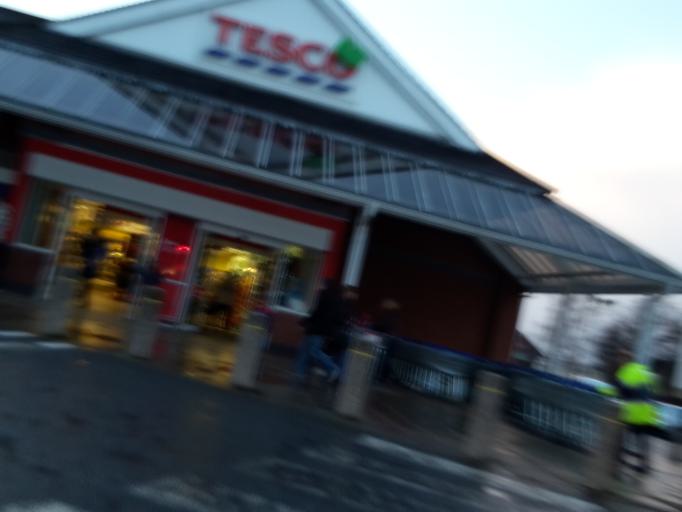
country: GB
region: Scotland
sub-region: South Lanarkshire
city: Uddingston
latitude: 55.8163
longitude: -4.0821
